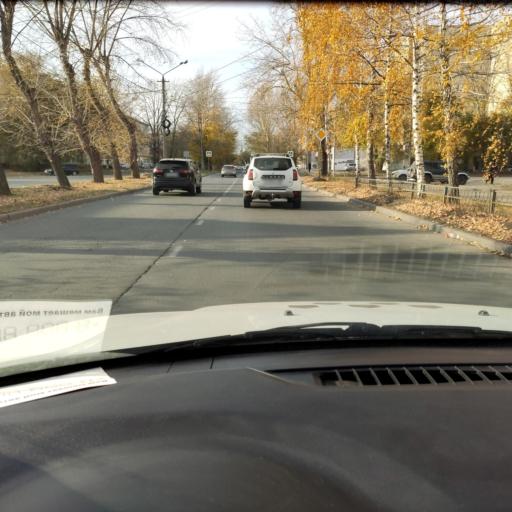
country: RU
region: Samara
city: Tol'yatti
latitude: 53.5173
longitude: 49.4295
